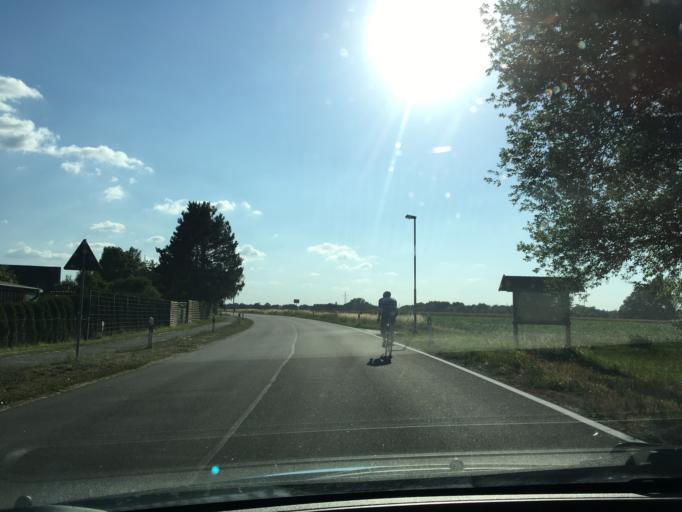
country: DE
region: Lower Saxony
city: Dahlenburg
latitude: 53.1844
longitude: 10.7298
